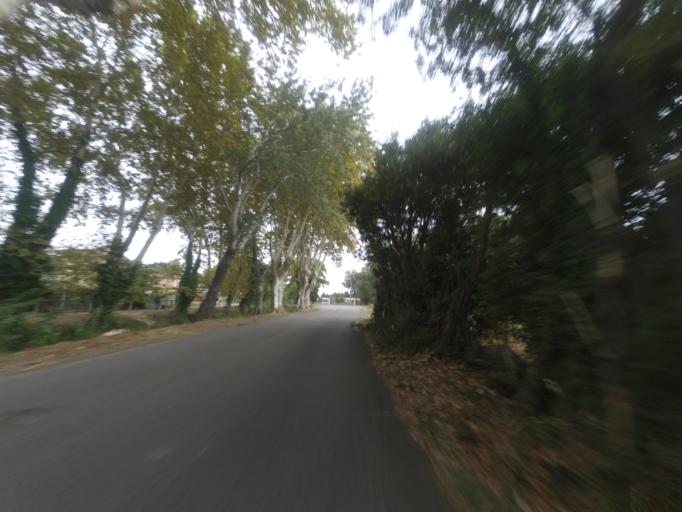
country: FR
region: Languedoc-Roussillon
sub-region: Departement des Pyrenees-Orientales
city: Saint-Esteve
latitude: 42.7047
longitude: 2.8516
